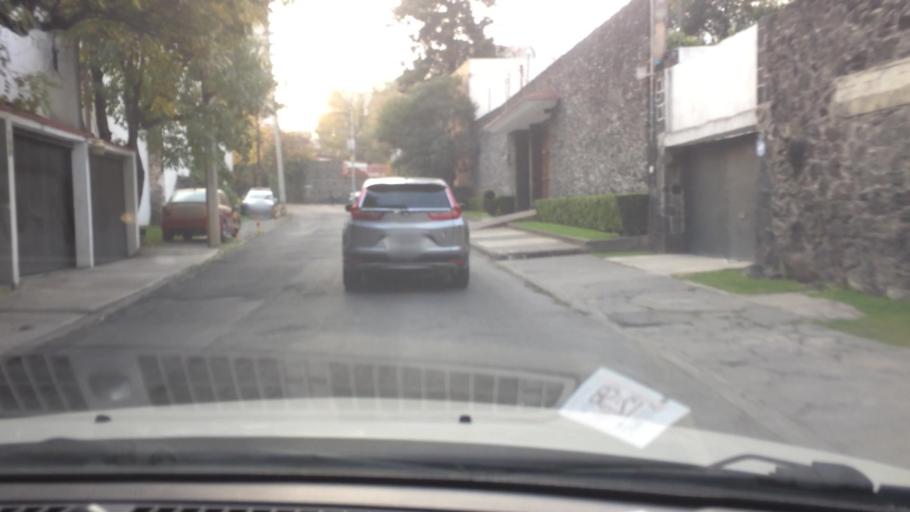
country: MX
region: Mexico City
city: Magdalena Contreras
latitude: 19.3239
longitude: -99.2131
